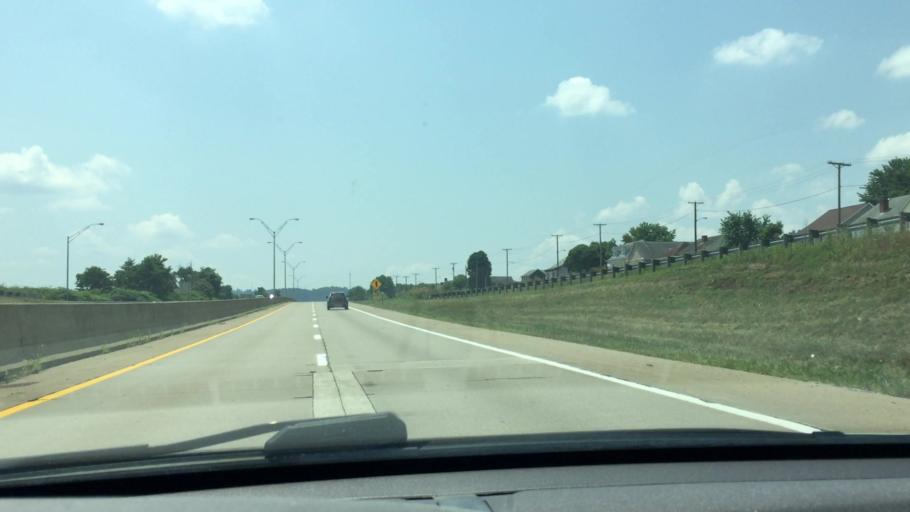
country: US
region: West Virginia
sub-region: Marshall County
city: Benwood
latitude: 40.0302
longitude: -80.7381
